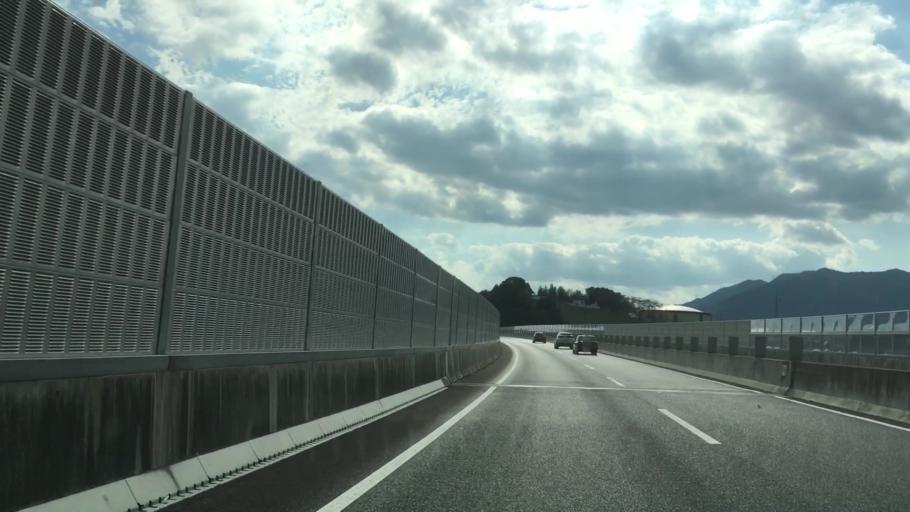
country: JP
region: Hiroshima
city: Hatsukaichi
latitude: 34.3566
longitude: 132.3245
